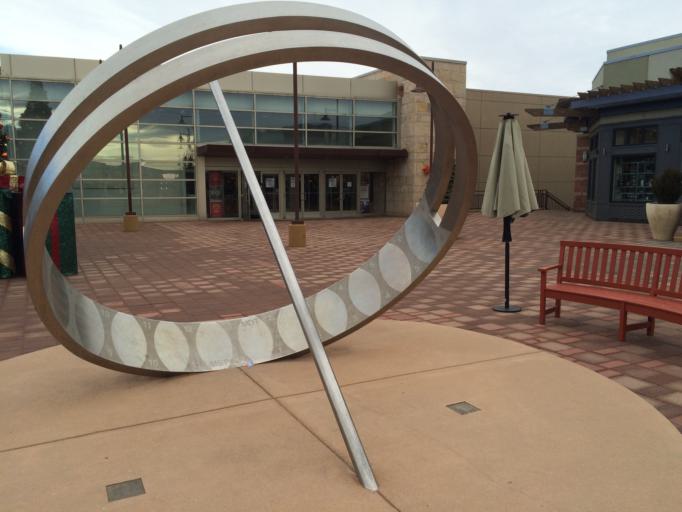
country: US
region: Colorado
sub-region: Boulder County
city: Boulder
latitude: 40.0192
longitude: -105.2559
